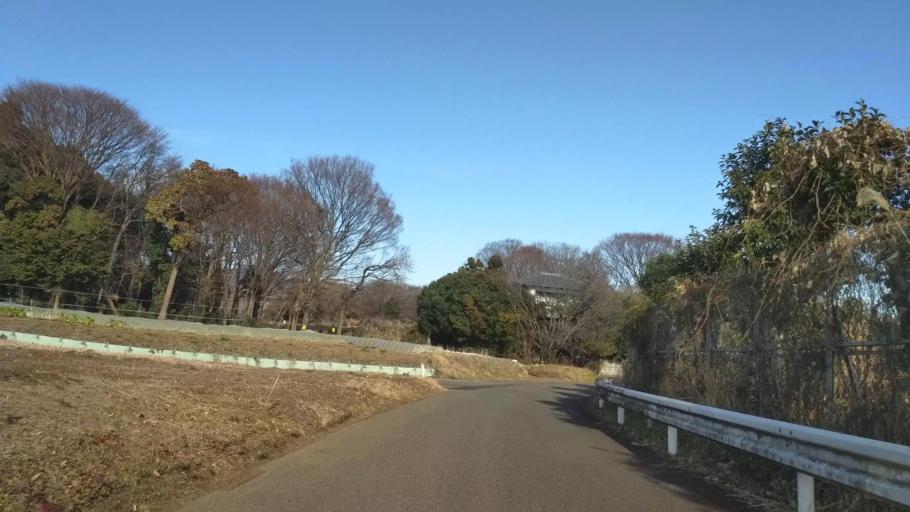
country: JP
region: Kanagawa
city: Hadano
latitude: 35.3534
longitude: 139.2337
